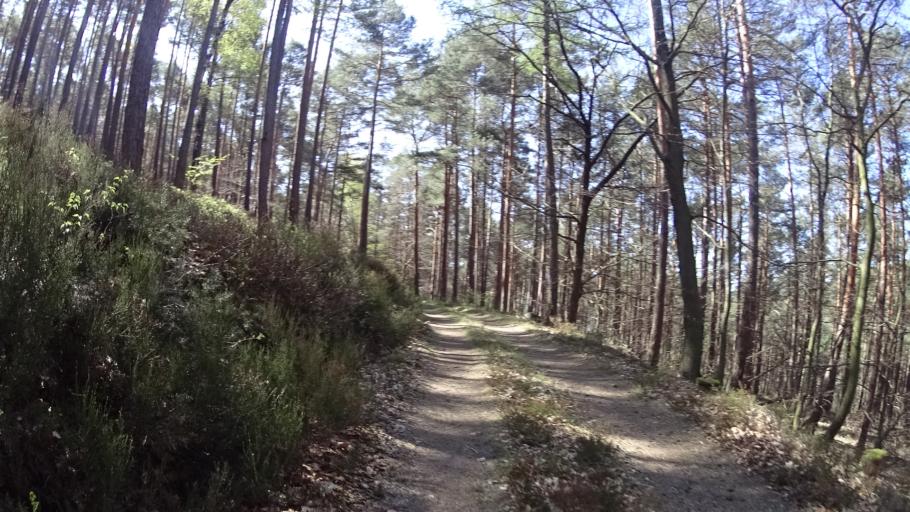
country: DE
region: Rheinland-Pfalz
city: Lambrecht
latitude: 49.3837
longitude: 8.0749
